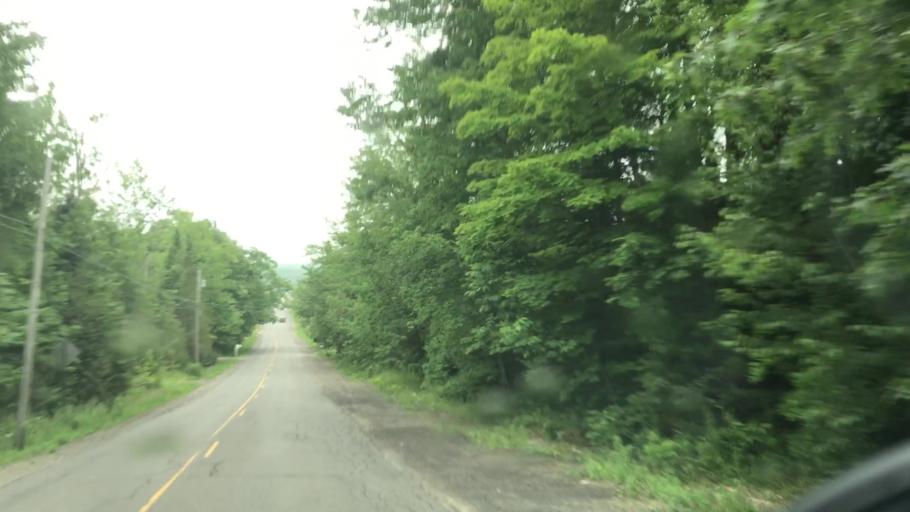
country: US
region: Maine
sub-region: Penobscot County
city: Veazie
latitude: 44.8762
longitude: -68.7132
